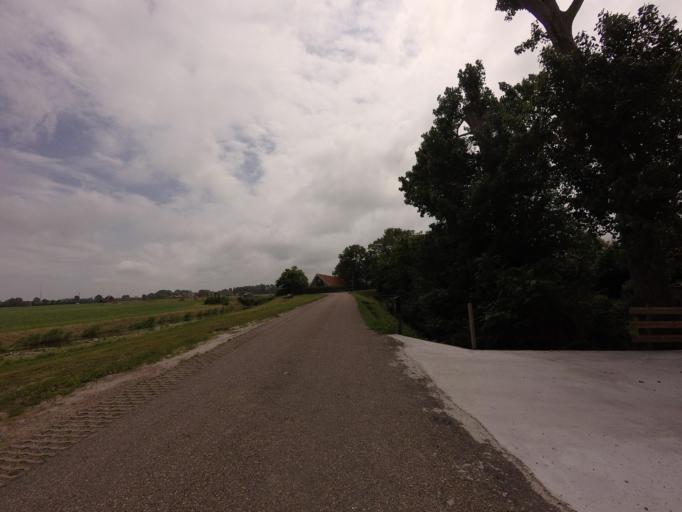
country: NL
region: North Holland
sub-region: Gemeente Schagen
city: Schagen
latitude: 52.7912
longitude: 4.7688
